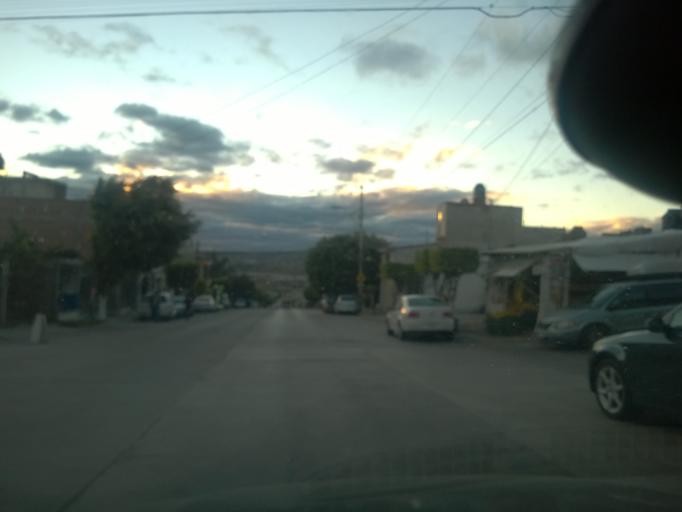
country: MX
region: Guanajuato
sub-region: Leon
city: La Ermita
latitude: 21.1536
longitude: -101.7329
